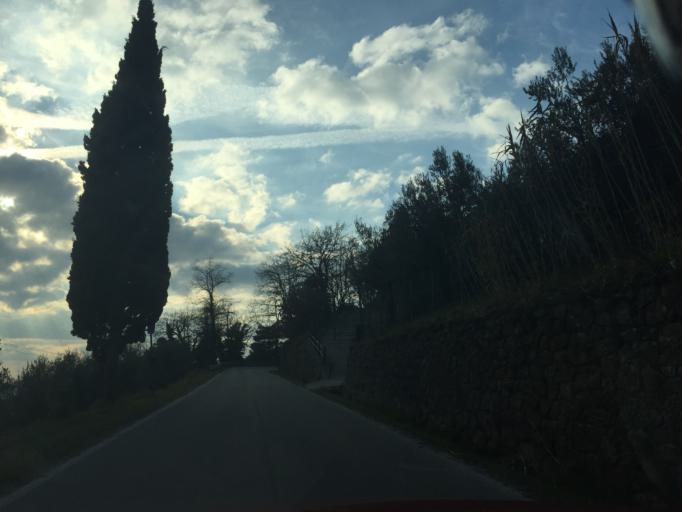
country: IT
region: Tuscany
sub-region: Provincia di Pistoia
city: Larciano
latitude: 43.8261
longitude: 10.9292
